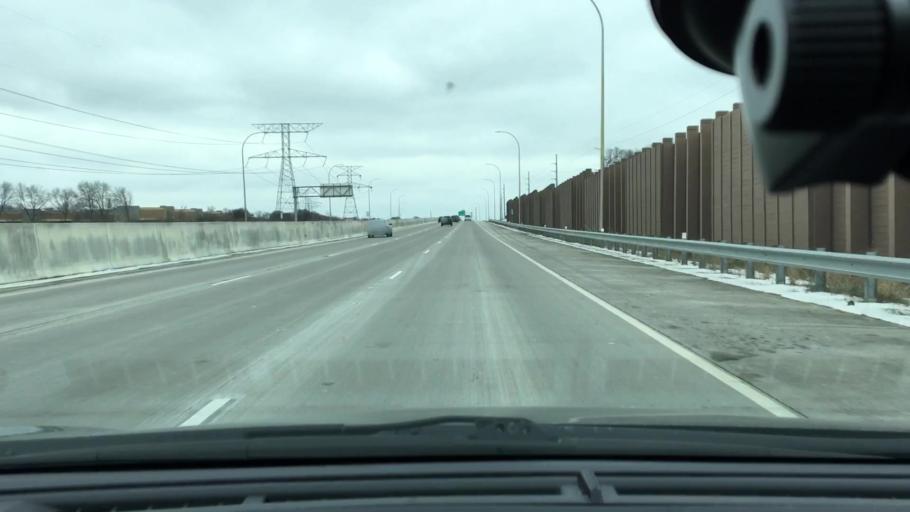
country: US
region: Minnesota
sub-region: Hennepin County
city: Plymouth
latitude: 45.0206
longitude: -93.4548
